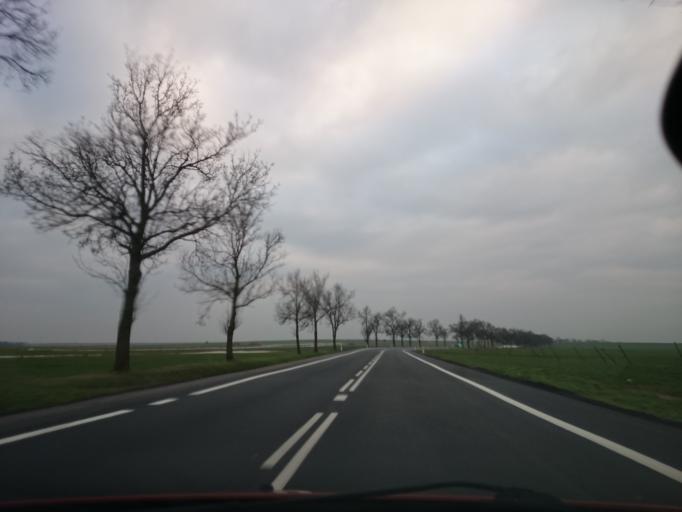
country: PL
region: Opole Voivodeship
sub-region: Powiat nyski
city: Sidzina
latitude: 50.5696
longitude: 17.4438
